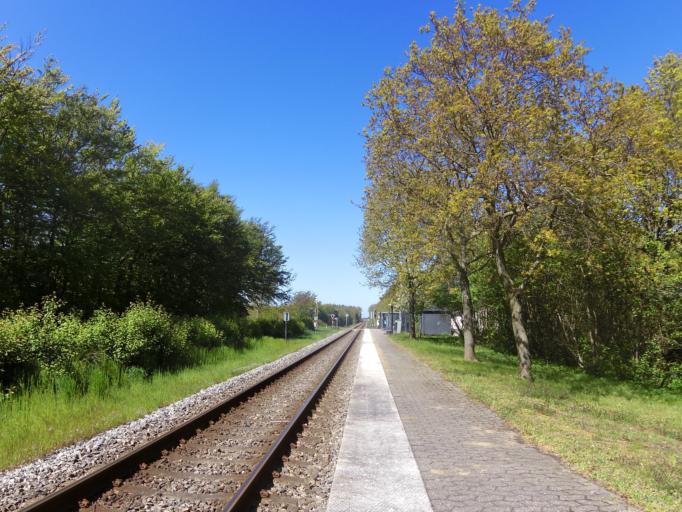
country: DK
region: South Denmark
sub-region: Tonder Kommune
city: Sherrebek
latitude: 55.2299
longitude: 8.7322
